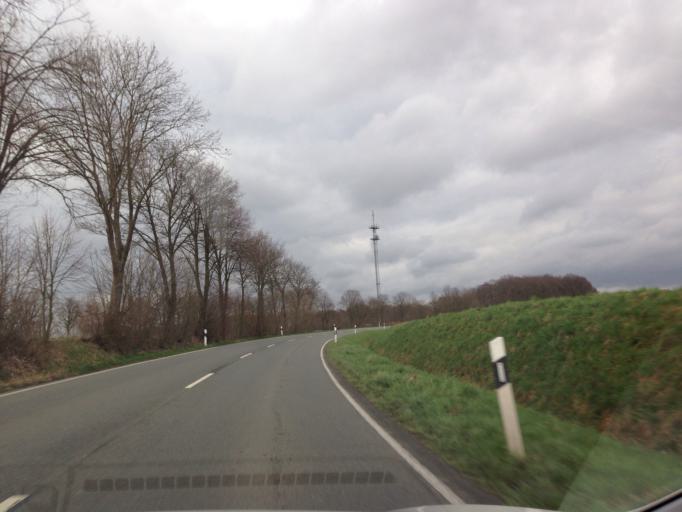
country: DE
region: North Rhine-Westphalia
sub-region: Regierungsbezirk Munster
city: Nordkirchen
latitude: 51.7587
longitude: 7.5247
